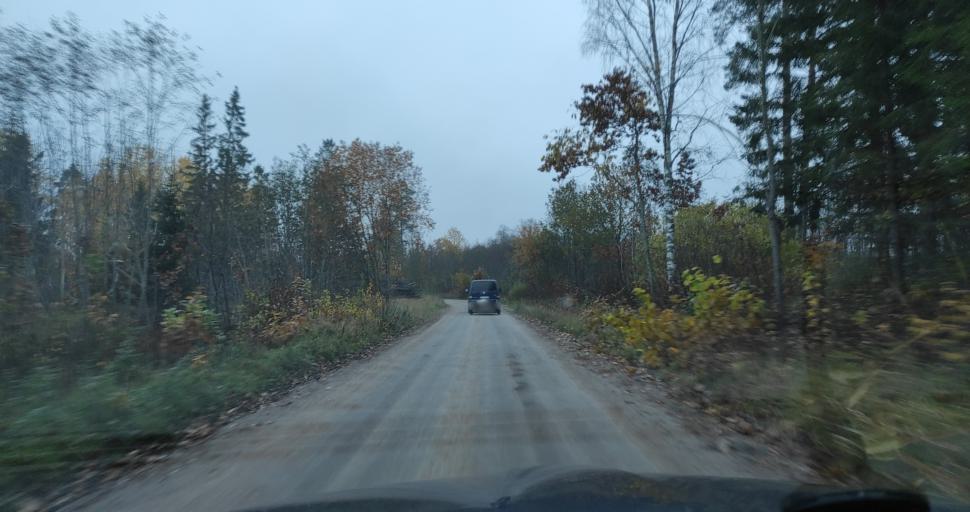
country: LV
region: Pavilostas
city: Pavilosta
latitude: 56.7612
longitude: 21.2737
